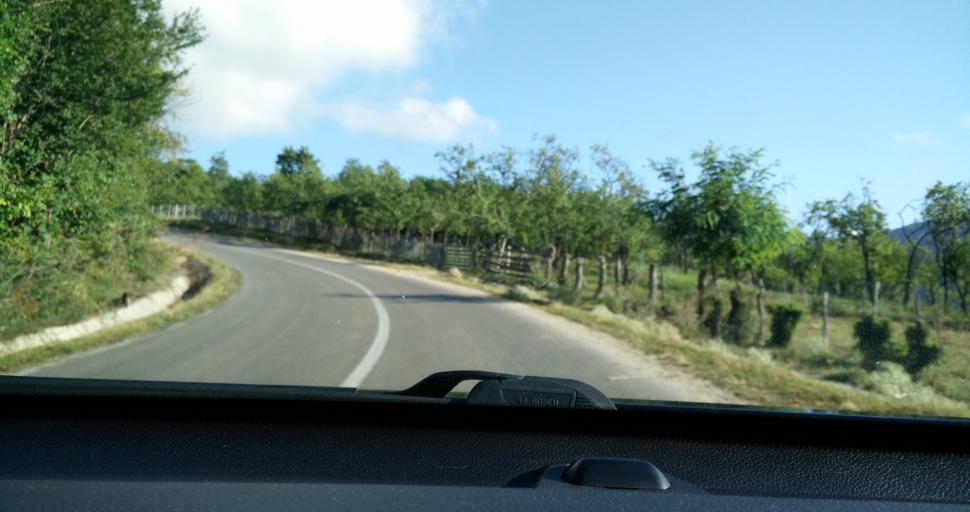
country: RO
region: Gorj
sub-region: Comuna Baia de Fier
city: Baia de Fier
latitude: 45.1766
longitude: 23.7813
